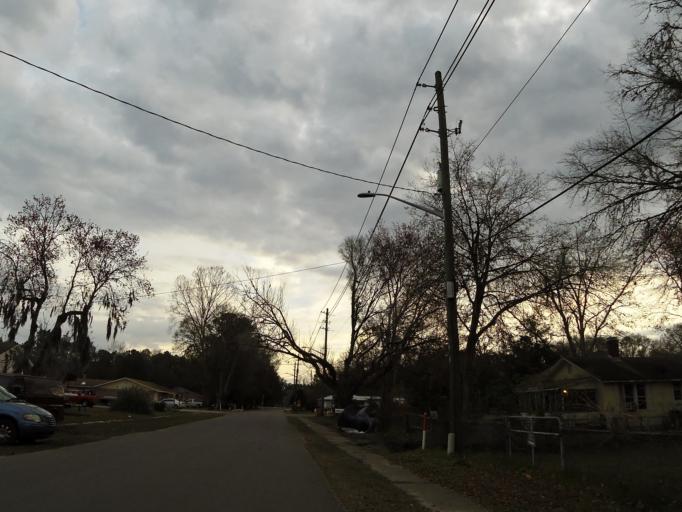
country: US
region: Florida
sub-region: Duval County
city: Baldwin
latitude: 30.3016
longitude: -81.9787
